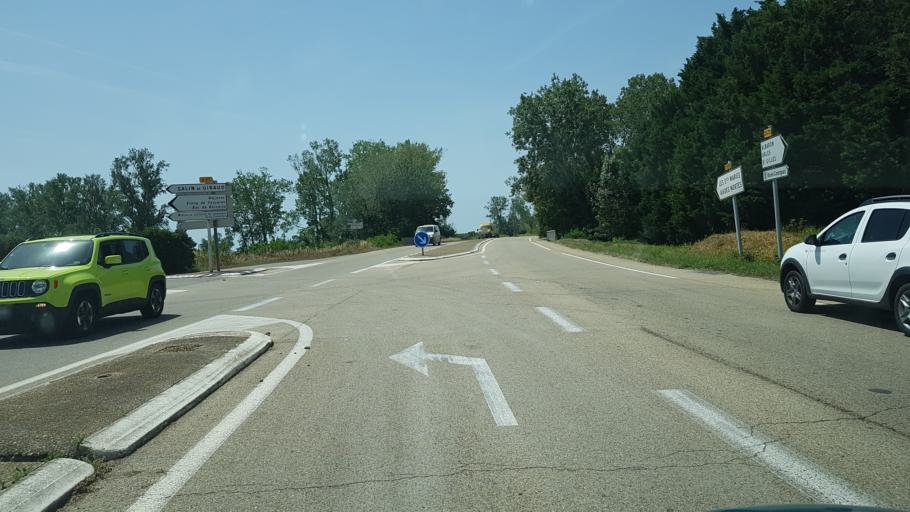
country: FR
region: Languedoc-Roussillon
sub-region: Departement du Gard
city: Saint-Gilles
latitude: 43.6090
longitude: 4.4779
